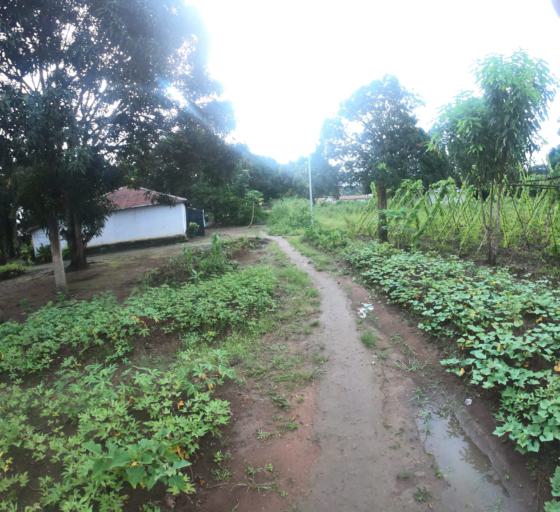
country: SL
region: Southern Province
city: Rotifunk
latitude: 8.4881
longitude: -12.7620
